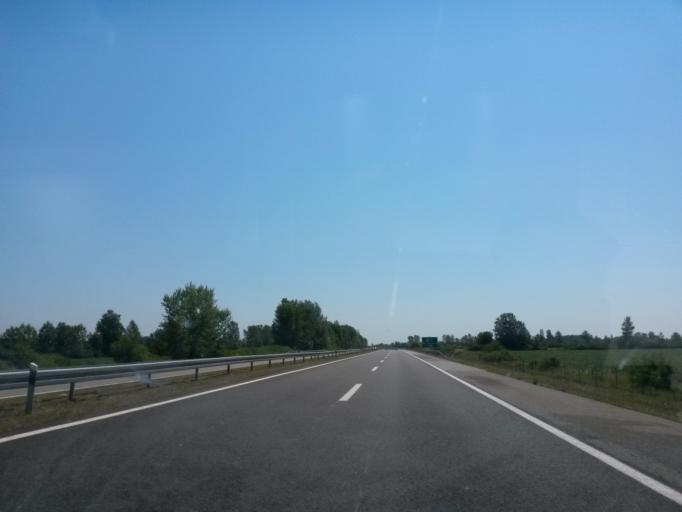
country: BA
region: Federation of Bosnia and Herzegovina
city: Donja Dubica
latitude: 45.1383
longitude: 18.3746
